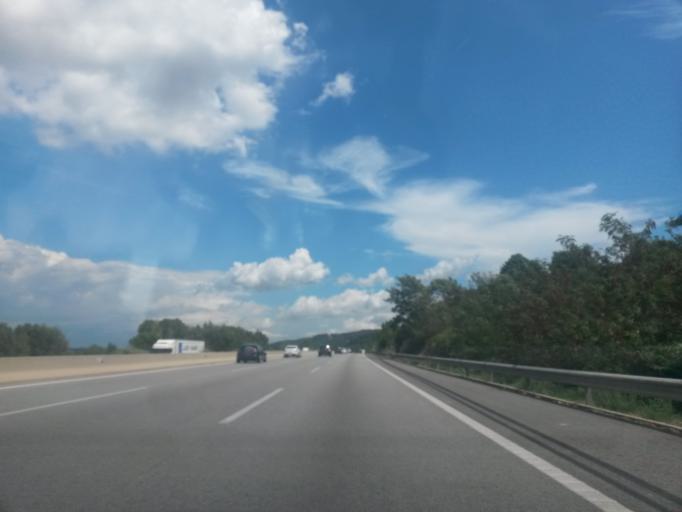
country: ES
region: Catalonia
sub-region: Provincia de Girona
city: Breda
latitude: 41.7129
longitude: 2.5435
